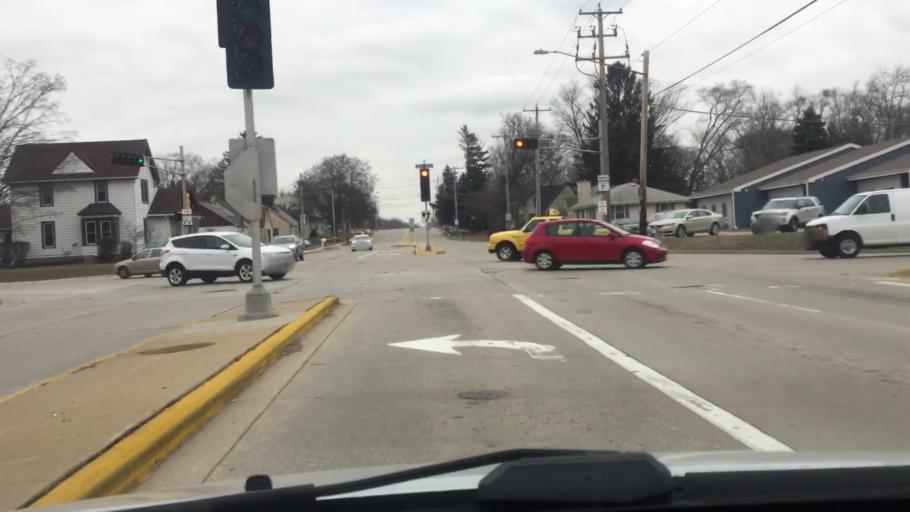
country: US
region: Wisconsin
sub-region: Waukesha County
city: Sussex
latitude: 43.1289
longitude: -88.2096
